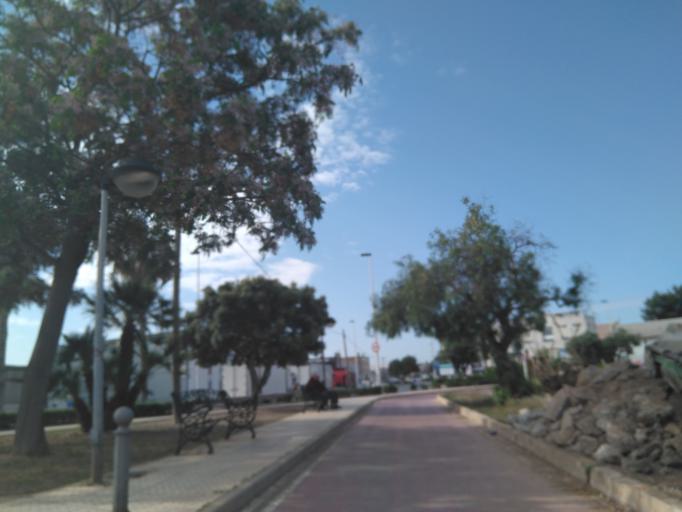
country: ES
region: Valencia
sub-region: Provincia de Valencia
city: Alboraya
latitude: 39.5034
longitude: -0.3460
